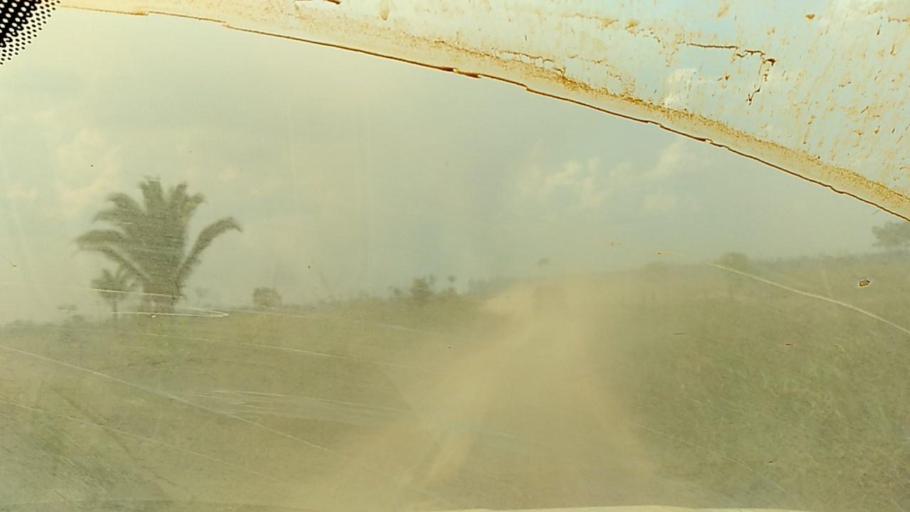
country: BR
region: Rondonia
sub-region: Porto Velho
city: Porto Velho
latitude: -8.6905
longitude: -63.2391
